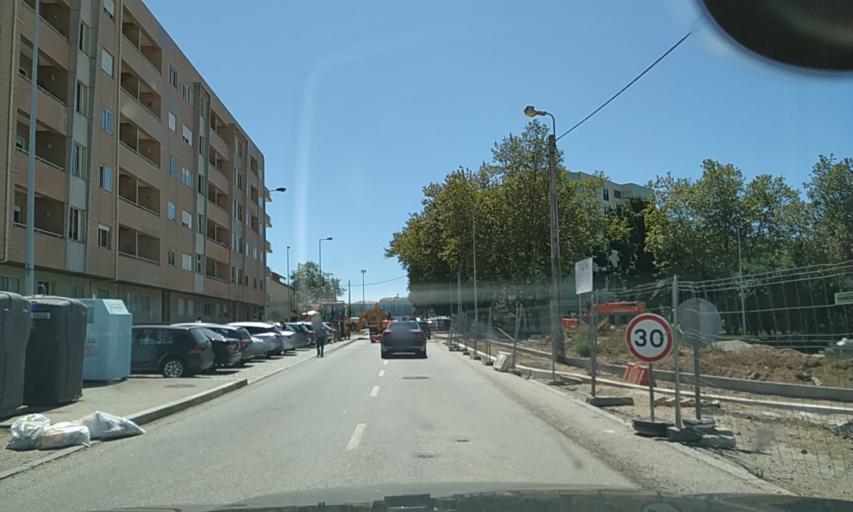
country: PT
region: Porto
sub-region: Vila Nova de Gaia
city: Canidelo
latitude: 41.1352
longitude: -8.6451
